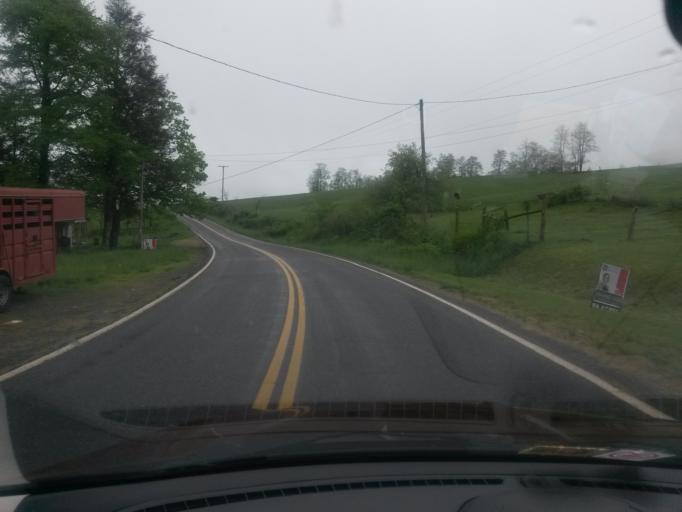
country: US
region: Virginia
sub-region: Floyd County
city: Floyd
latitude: 36.7660
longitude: -80.3915
